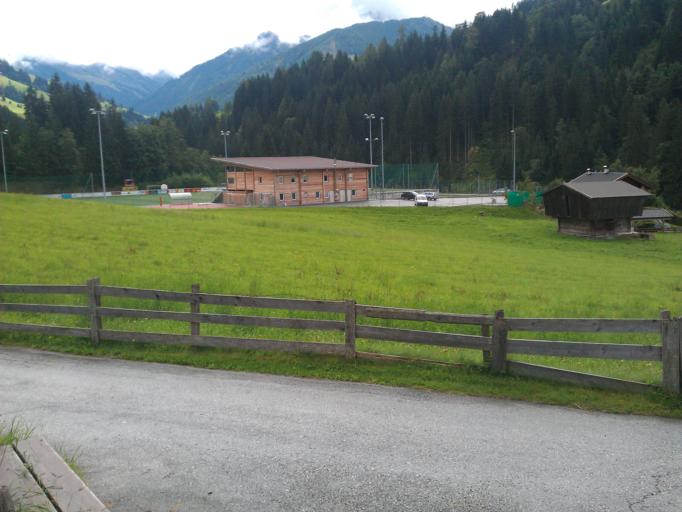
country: AT
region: Tyrol
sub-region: Politischer Bezirk Kufstein
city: Alpbach
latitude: 47.3958
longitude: 11.9416
